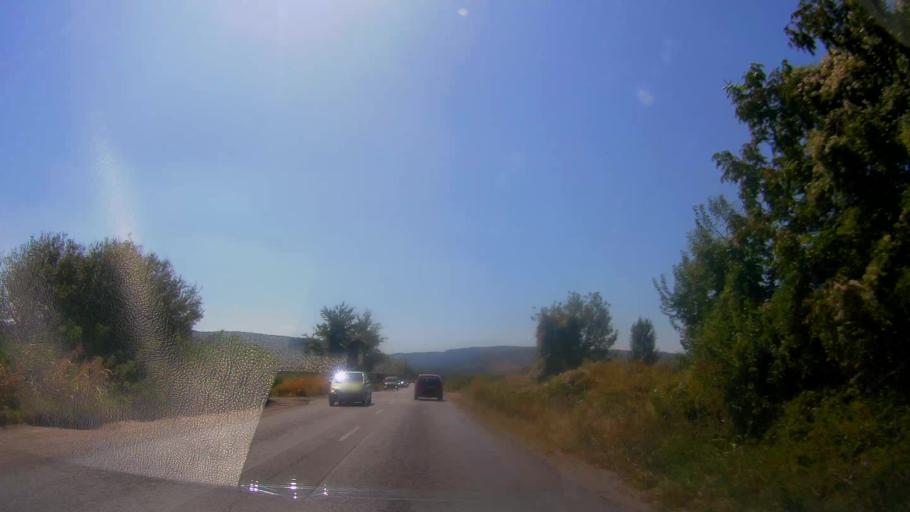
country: BG
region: Veliko Turnovo
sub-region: Obshtina Gorna Oryakhovitsa
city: Purvomaytsi
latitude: 43.1571
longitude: 25.6190
